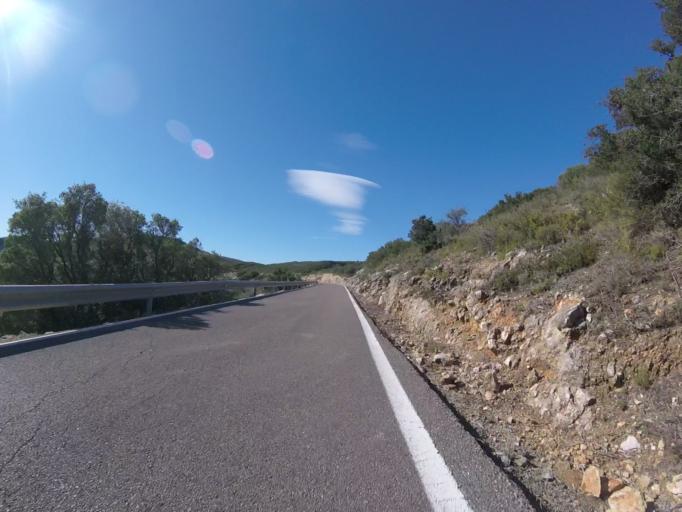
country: ES
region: Valencia
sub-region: Provincia de Castello
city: Albocasser
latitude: 40.3956
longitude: 0.0415
